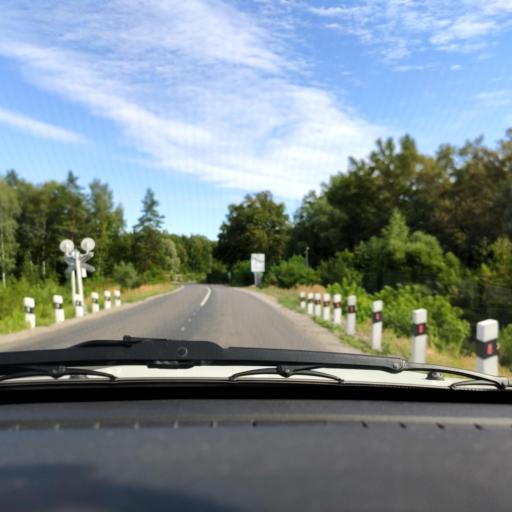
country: RU
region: Voronezj
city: Krasnolesnyy
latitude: 51.8670
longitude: 39.6682
